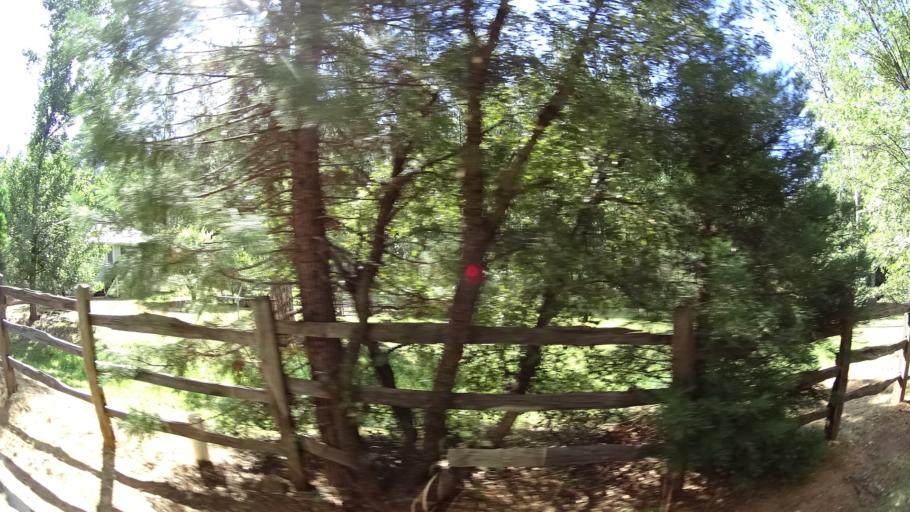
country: US
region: California
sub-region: Amador County
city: Pioneer
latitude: 38.3922
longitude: -120.4437
